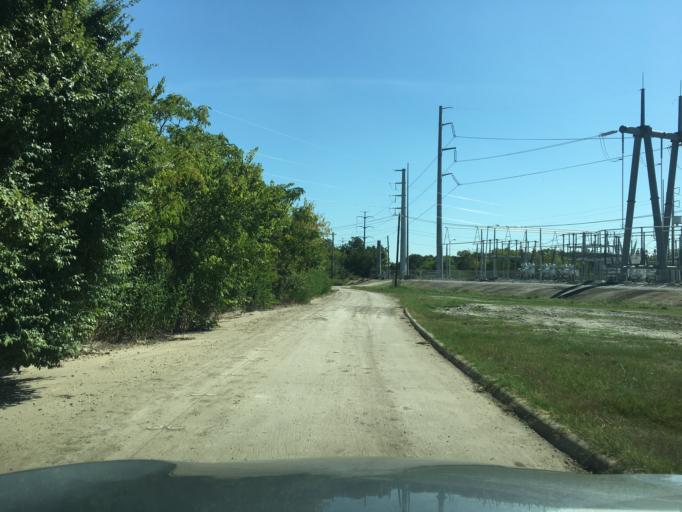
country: US
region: Texas
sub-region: Dallas County
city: Sachse
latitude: 32.9584
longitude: -96.6134
